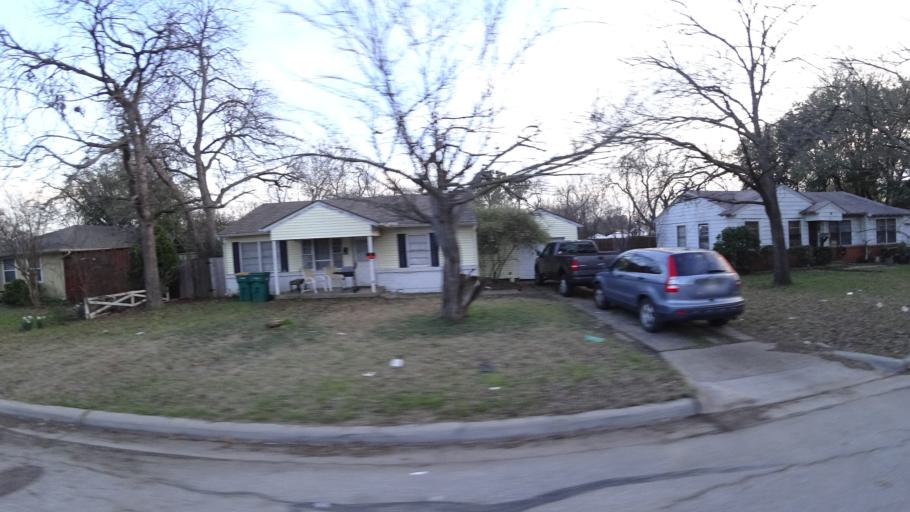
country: US
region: Texas
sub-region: Denton County
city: Lewisville
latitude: 33.0446
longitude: -96.9999
